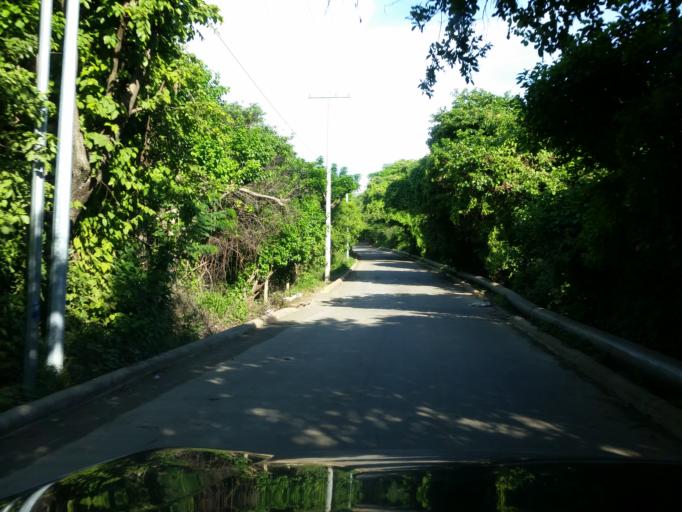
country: NI
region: Managua
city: Managua
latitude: 12.1009
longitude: -86.2166
